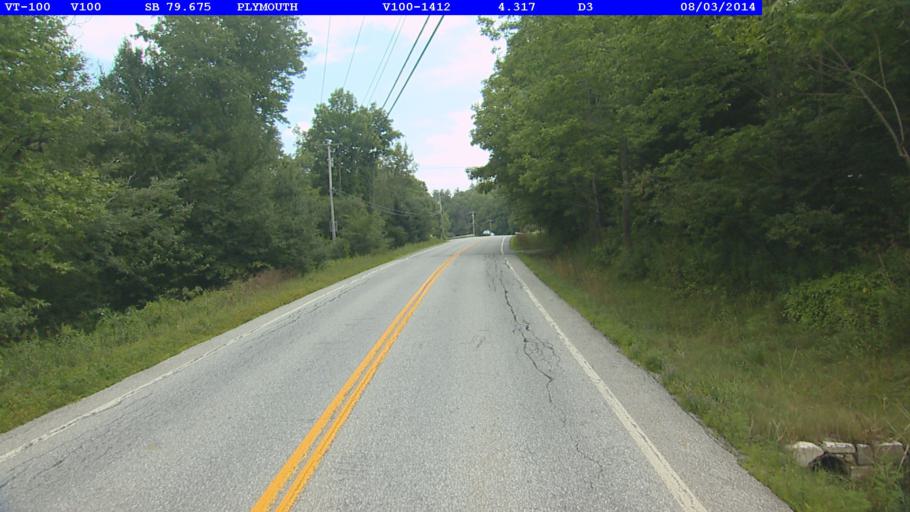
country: US
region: Vermont
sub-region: Windsor County
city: Woodstock
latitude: 43.5169
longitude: -72.7319
